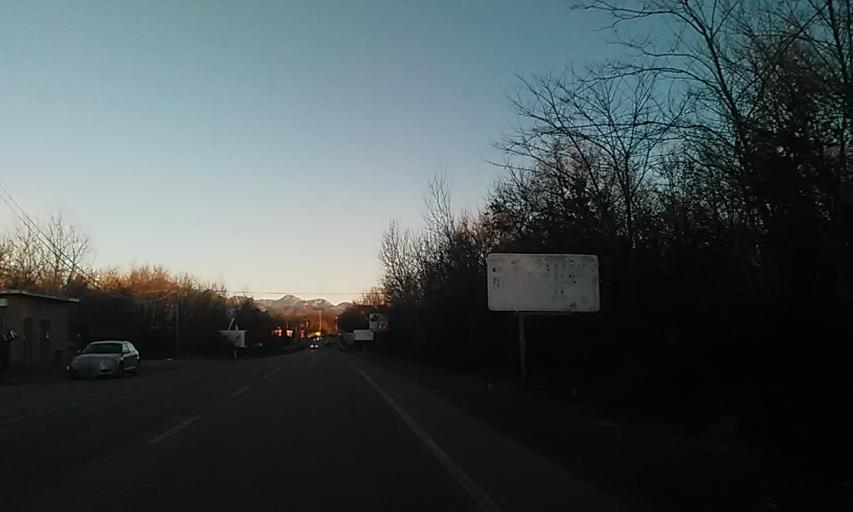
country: IT
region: Piedmont
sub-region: Provincia di Biella
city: Brusnengo
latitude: 45.5568
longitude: 8.2417
